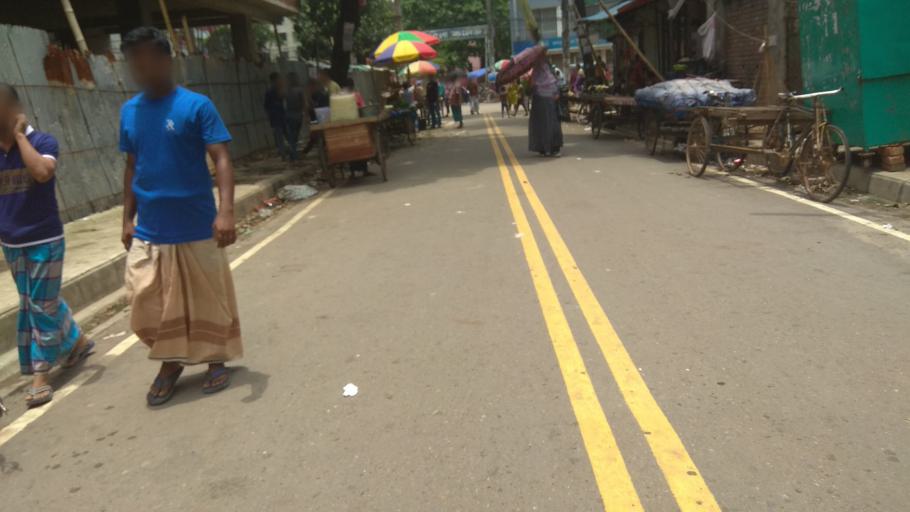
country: BD
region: Dhaka
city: Tungi
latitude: 23.8160
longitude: 90.3561
